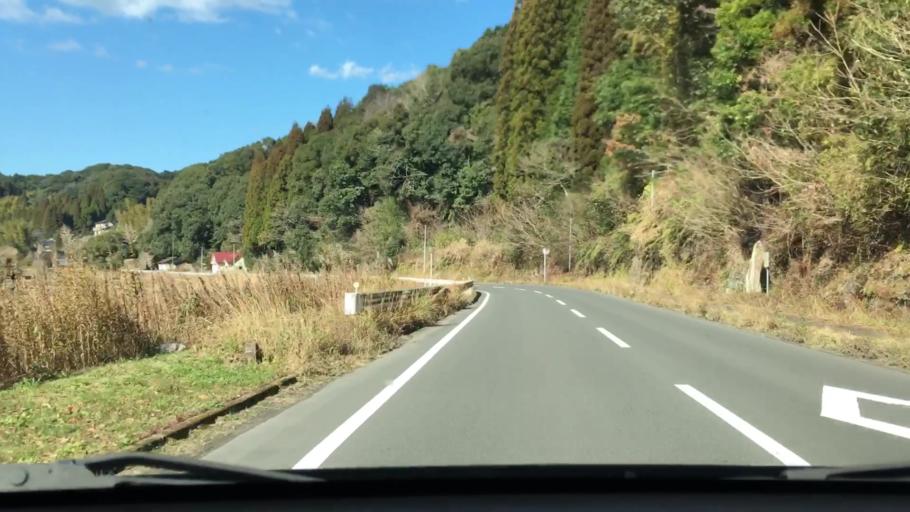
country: JP
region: Kagoshima
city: Ijuin
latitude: 31.6971
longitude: 130.4610
